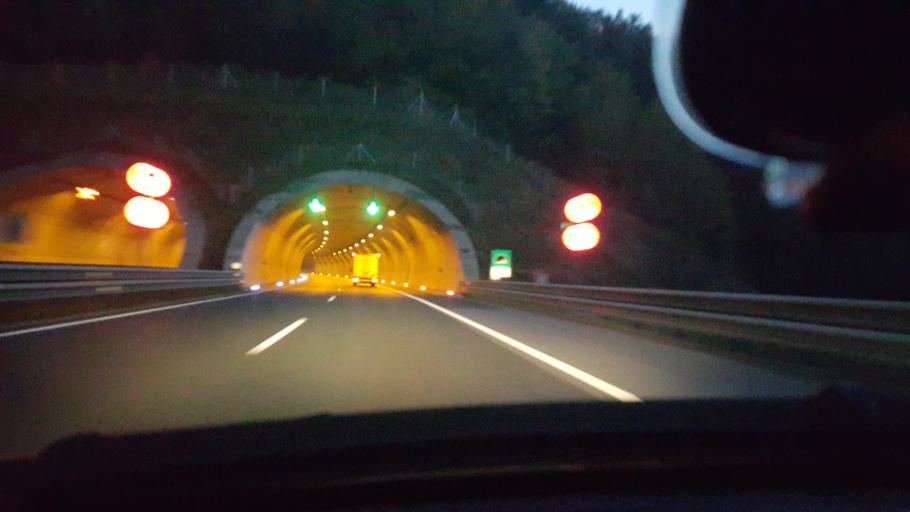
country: SI
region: Pesnica
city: Pesnica pri Mariboru
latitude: 46.5673
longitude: 15.6858
